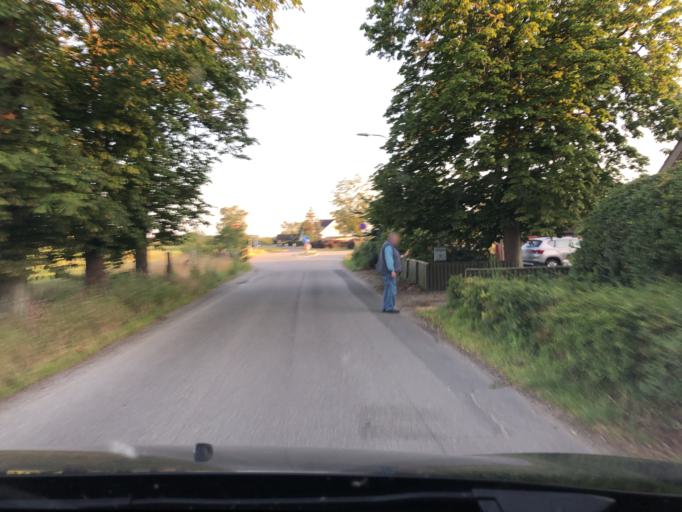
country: DK
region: South Denmark
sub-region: Fredericia Kommune
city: Fredericia
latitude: 55.6295
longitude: 9.7402
